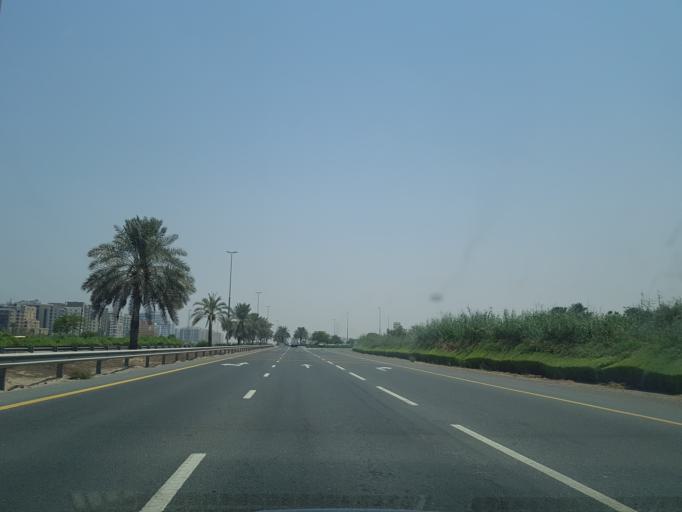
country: AE
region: Dubai
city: Dubai
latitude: 25.1120
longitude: 55.3908
